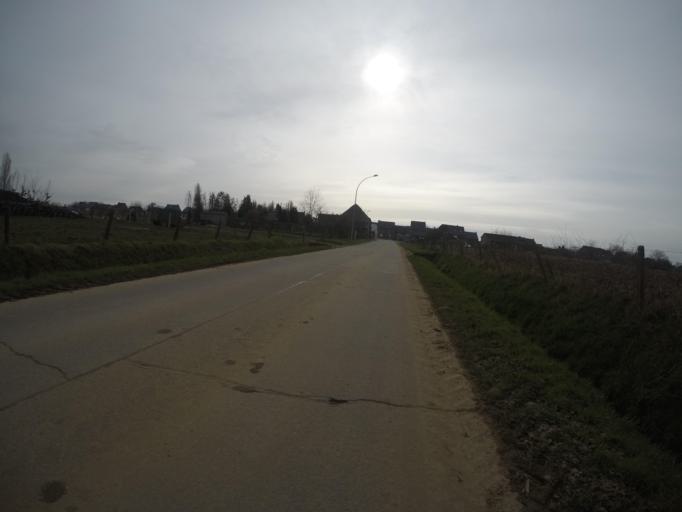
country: BE
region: Flanders
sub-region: Provincie Oost-Vlaanderen
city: Sint-Maria-Lierde
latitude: 50.8033
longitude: 3.8161
